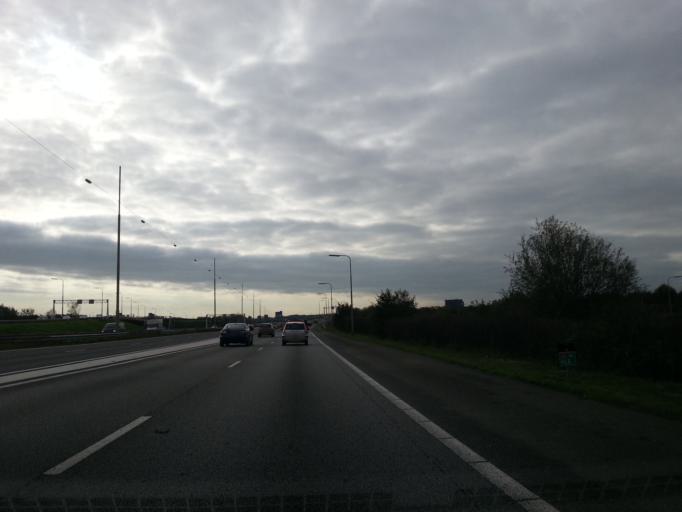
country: NL
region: South Holland
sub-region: Gemeente Den Haag
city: Ypenburg
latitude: 52.0570
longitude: 4.3693
